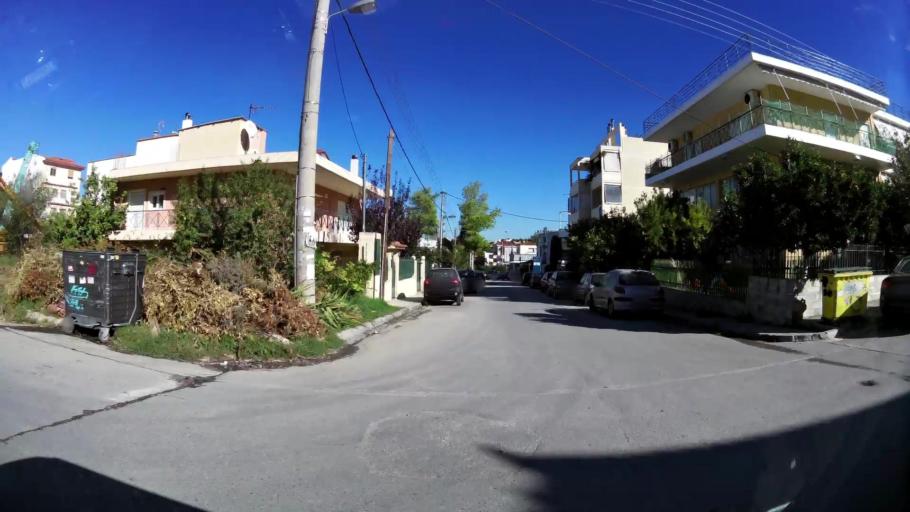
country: GR
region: Attica
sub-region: Nomarchia Anatolikis Attikis
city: Leondarion
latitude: 37.9862
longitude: 23.8494
